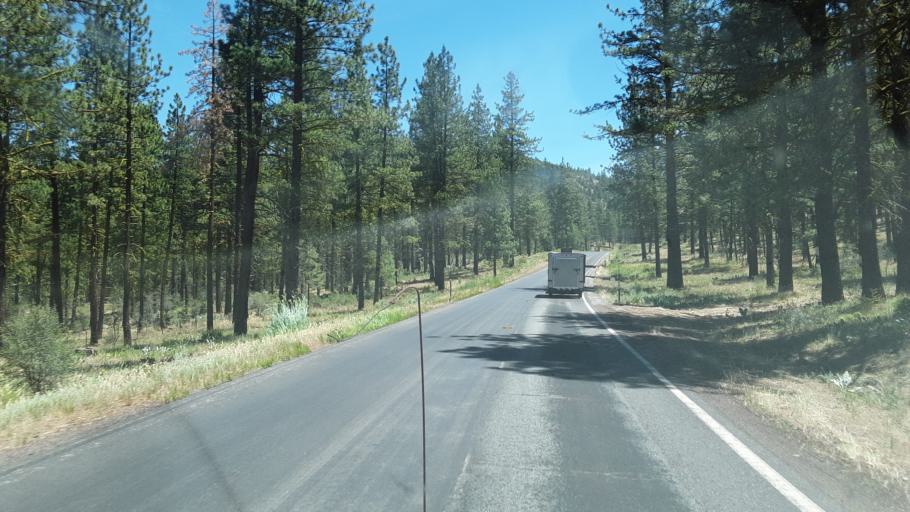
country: US
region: California
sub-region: Modoc County
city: Alturas
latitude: 40.9763
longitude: -120.7795
